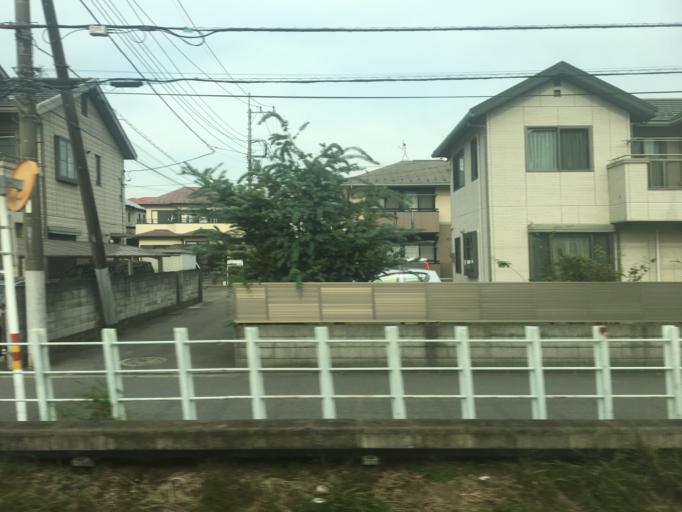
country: JP
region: Saitama
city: Kawagoe
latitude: 35.9058
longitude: 139.4752
